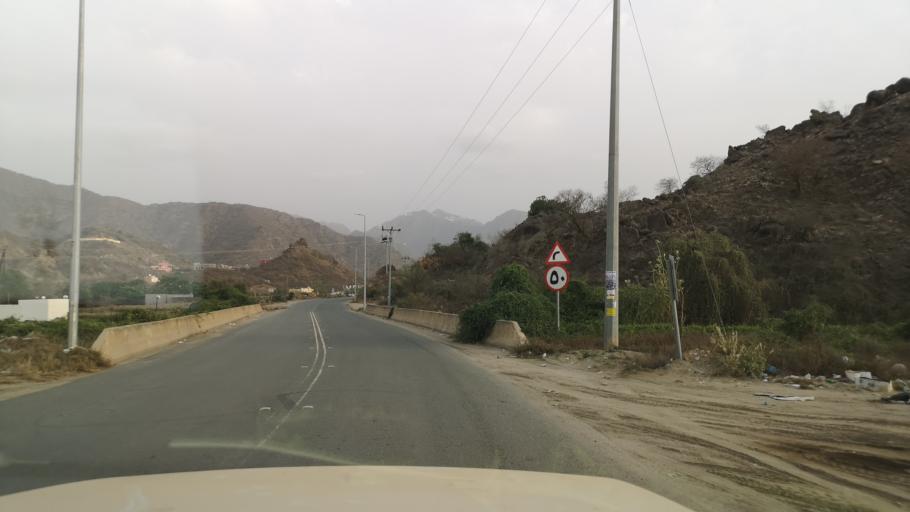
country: YE
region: Sa'dah
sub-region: Monabbih
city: Suq al Khamis
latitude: 17.3669
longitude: 43.1259
